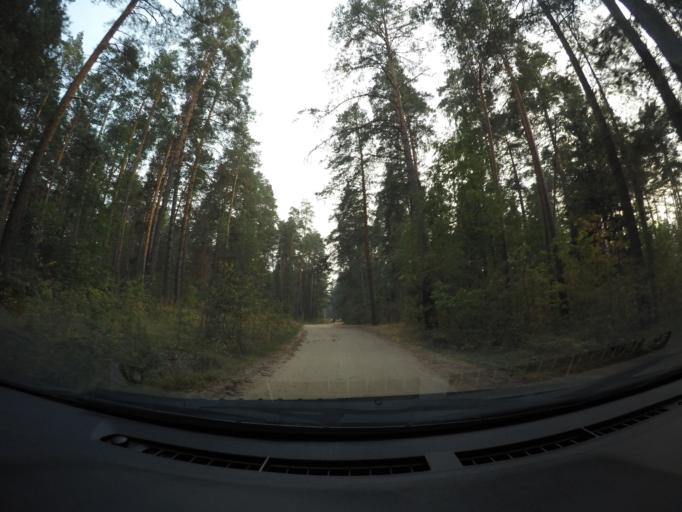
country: RU
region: Moskovskaya
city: Imeni Tsyurupy
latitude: 55.5051
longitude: 38.6930
